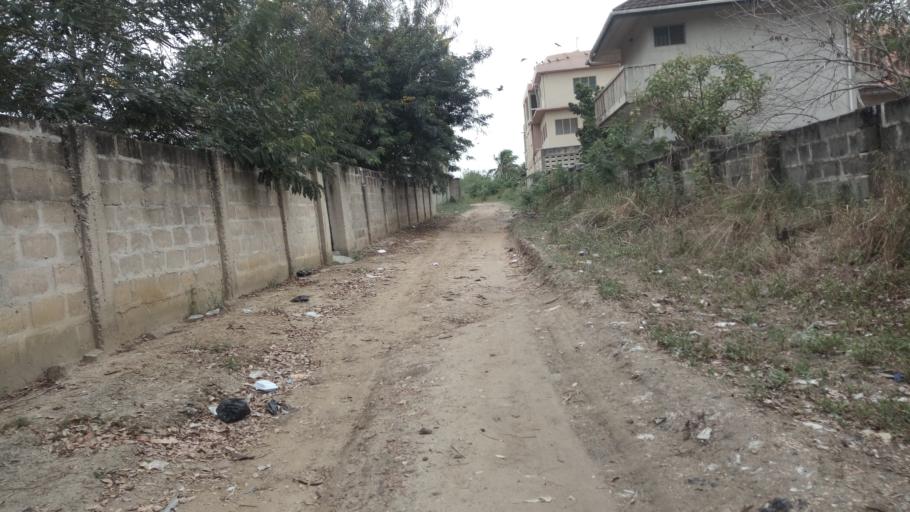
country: GH
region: Central
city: Winneba
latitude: 5.3666
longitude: -0.6385
